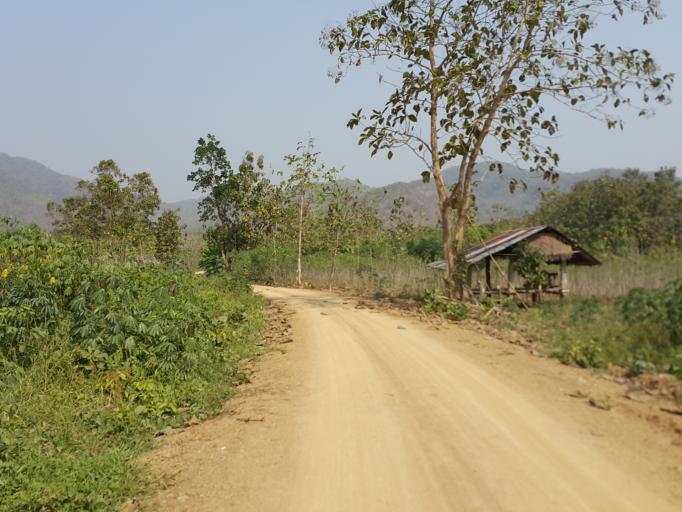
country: TH
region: Sukhothai
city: Thung Saliam
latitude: 17.3388
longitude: 99.4646
